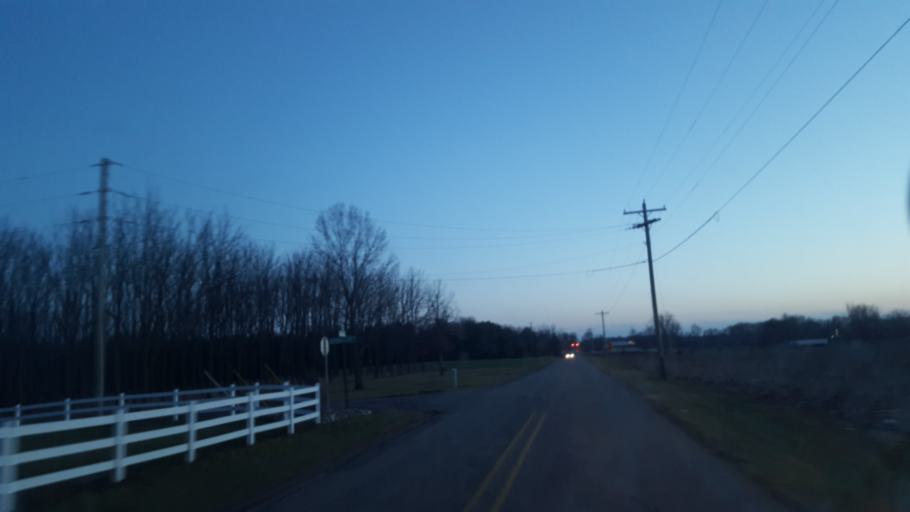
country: US
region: Indiana
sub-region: Kosciusko County
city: Mentone
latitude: 41.2719
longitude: -85.9987
